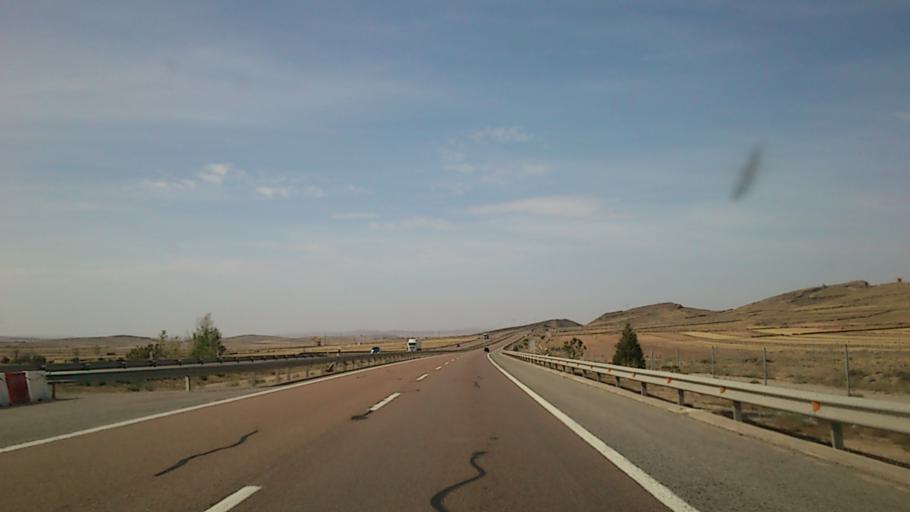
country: ES
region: Aragon
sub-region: Provincia de Teruel
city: Singra
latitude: 40.6433
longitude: -1.3150
